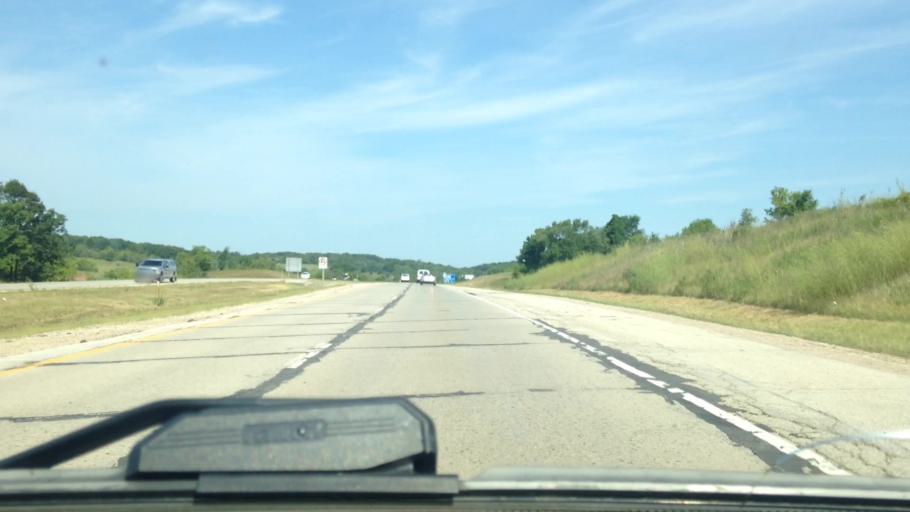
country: US
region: Wisconsin
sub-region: Washington County
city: West Bend
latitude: 43.4053
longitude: -88.1961
